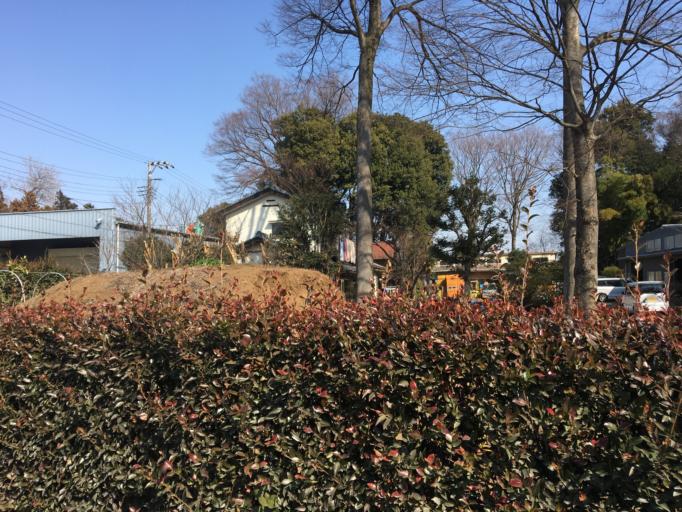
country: JP
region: Saitama
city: Oi
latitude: 35.8312
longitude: 139.5023
